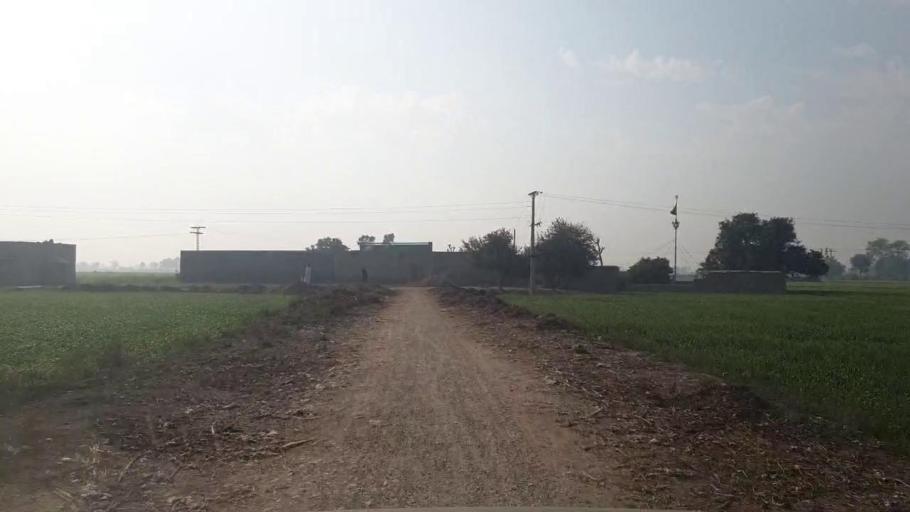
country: PK
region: Sindh
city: Hala
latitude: 25.8570
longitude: 68.4340
